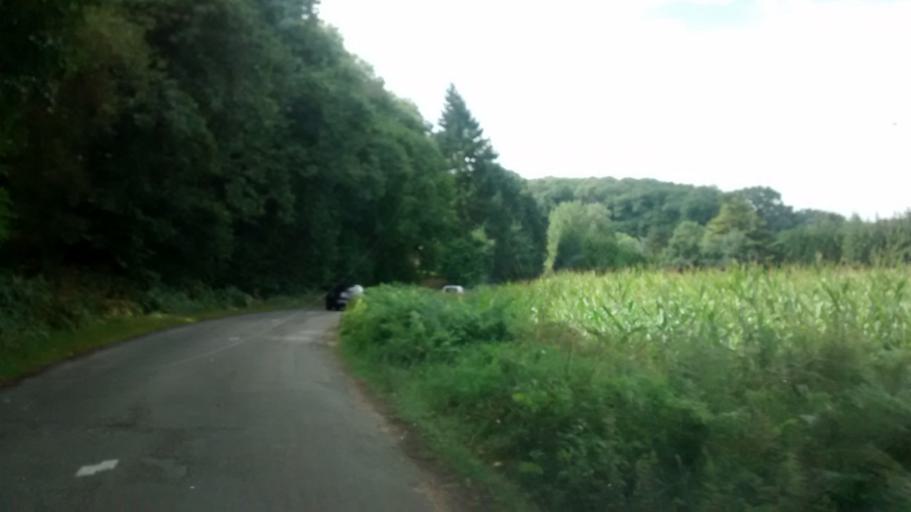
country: FR
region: Brittany
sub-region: Departement d'Ille-et-Vilaine
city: Tinteniac
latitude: 48.2913
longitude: -1.8471
